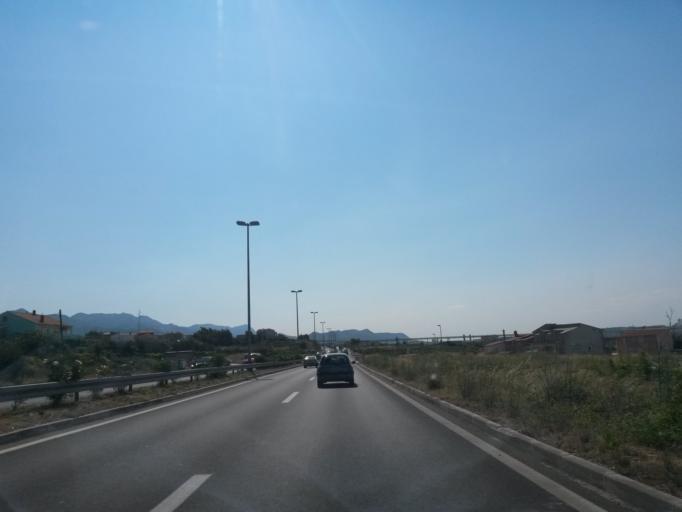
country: HR
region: Splitsko-Dalmatinska
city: Vranjic
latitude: 43.5486
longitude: 16.4409
